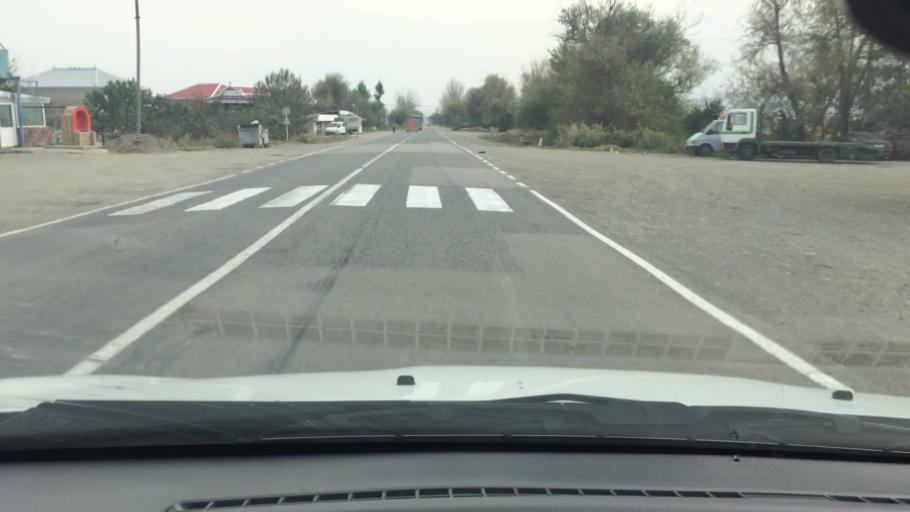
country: GE
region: Kvemo Kartli
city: Rust'avi
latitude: 41.4506
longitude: 44.9936
